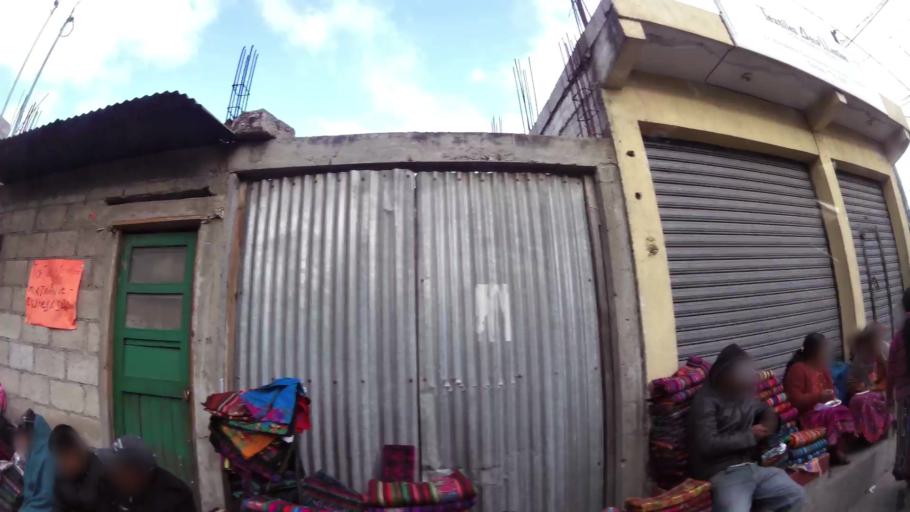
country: GT
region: Quetzaltenango
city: Salcaja
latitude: 14.8790
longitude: -91.4586
